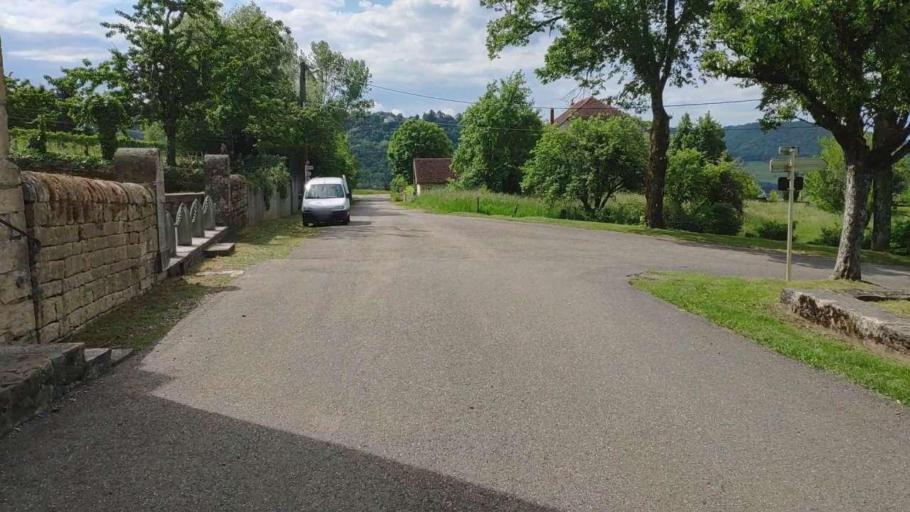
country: FR
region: Franche-Comte
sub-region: Departement du Jura
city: Perrigny
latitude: 46.7675
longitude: 5.6214
